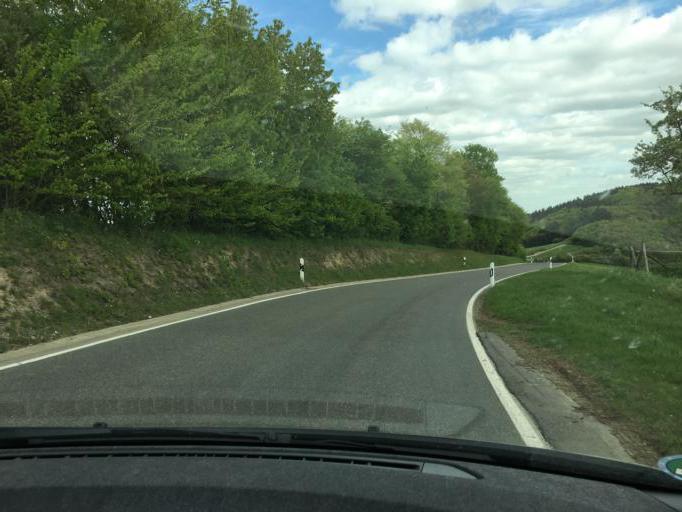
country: DE
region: Rheinland-Pfalz
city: Lind
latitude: 50.4969
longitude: 6.9428
